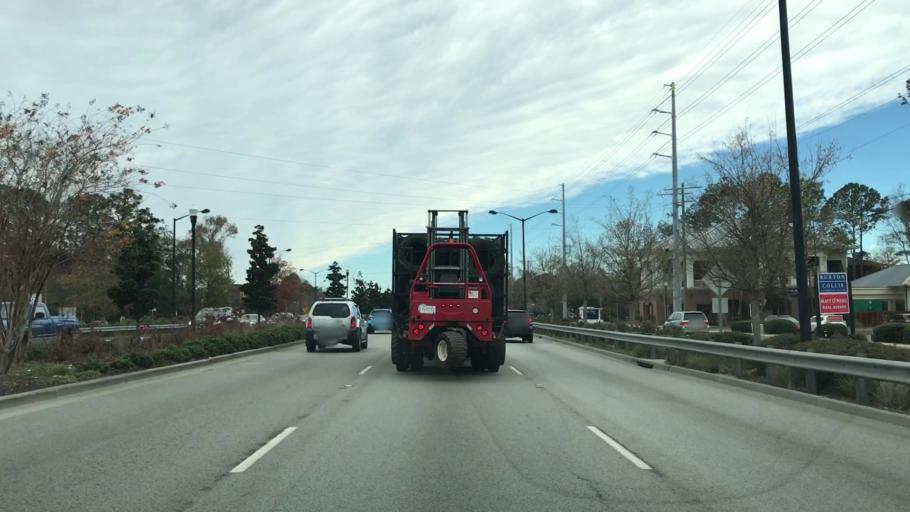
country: US
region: South Carolina
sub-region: Charleston County
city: Mount Pleasant
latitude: 32.8114
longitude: -79.8666
